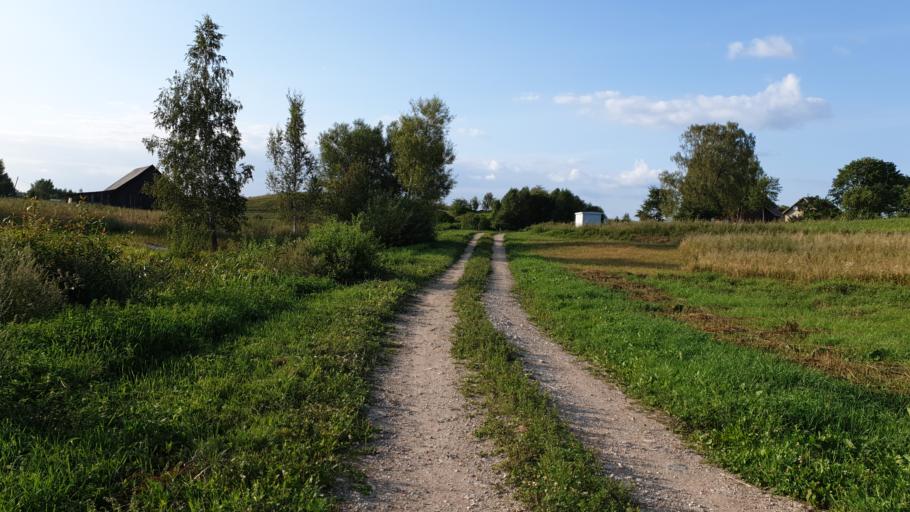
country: LT
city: Grigiskes
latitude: 54.7727
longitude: 25.0325
